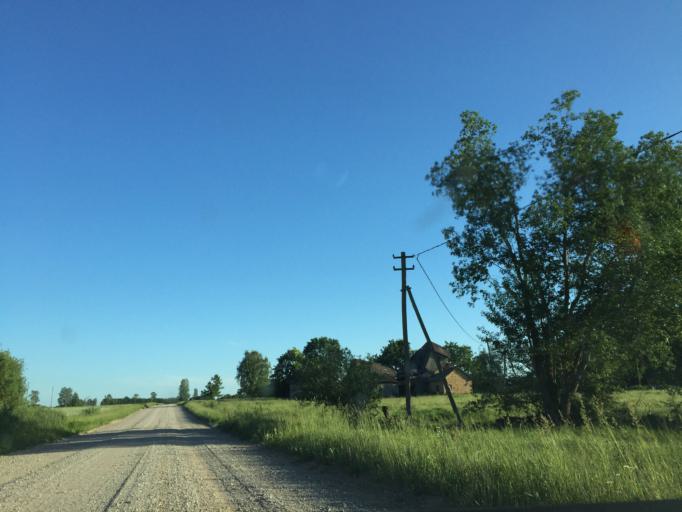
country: LV
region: Broceni
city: Broceni
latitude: 56.8167
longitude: 22.5462
